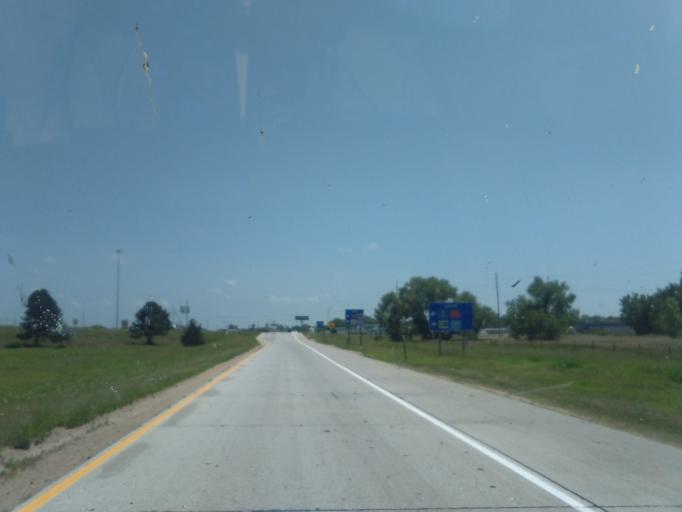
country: US
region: Nebraska
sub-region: Dawson County
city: Lexington
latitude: 40.7418
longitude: -99.7434
